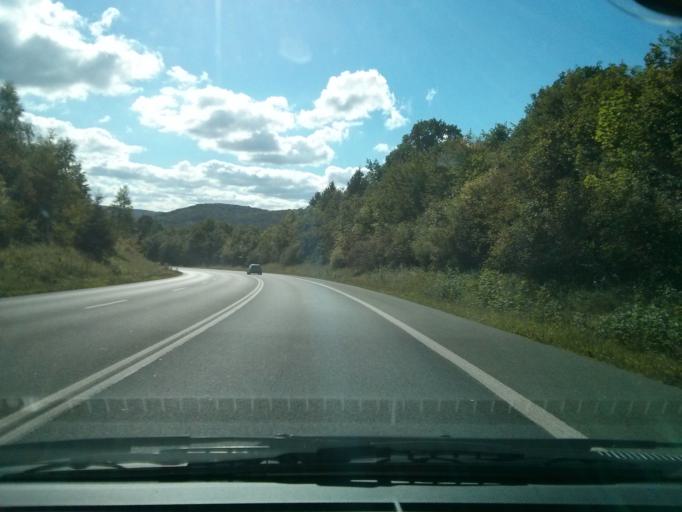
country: DE
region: North Rhine-Westphalia
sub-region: Regierungsbezirk Arnsberg
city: Arnsberg
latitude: 51.4197
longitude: 8.0550
